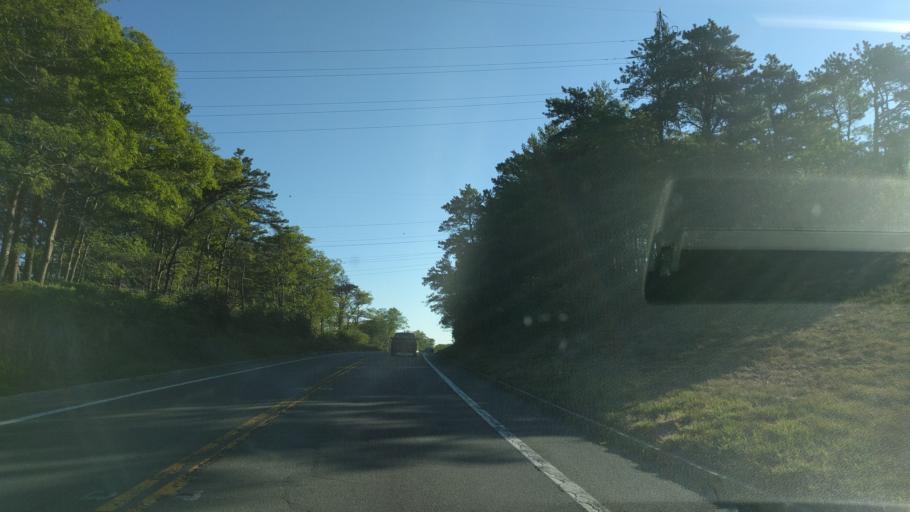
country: US
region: Massachusetts
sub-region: Barnstable County
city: Sagamore
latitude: 41.7659
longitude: -70.5646
